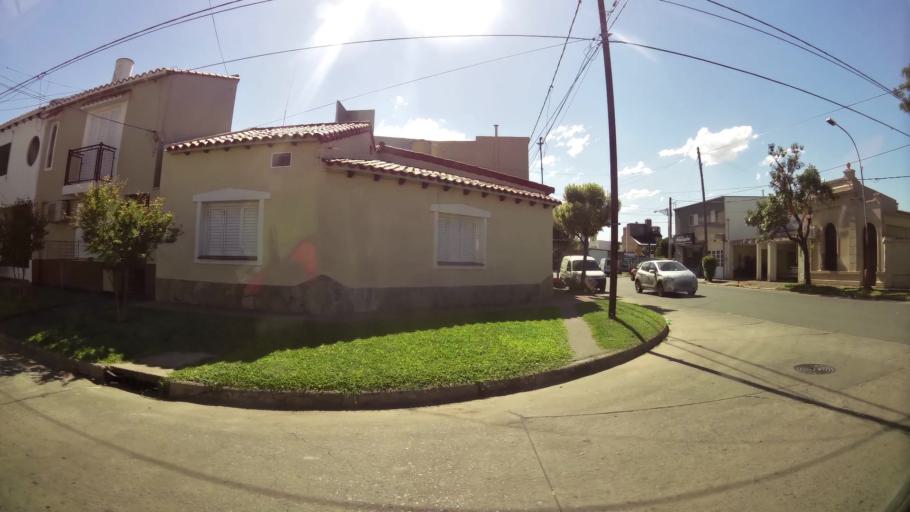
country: AR
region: Santa Fe
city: Santa Fe de la Vera Cruz
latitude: -31.6129
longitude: -60.6781
